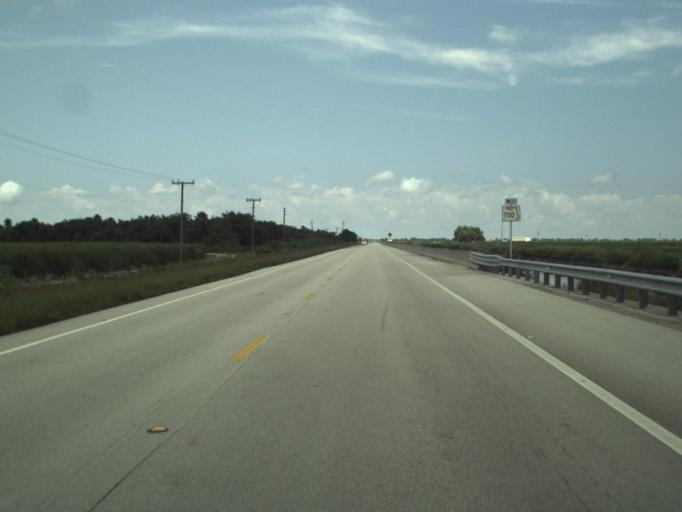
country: US
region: Florida
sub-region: Palm Beach County
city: Pahokee
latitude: 26.8335
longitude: -80.5908
